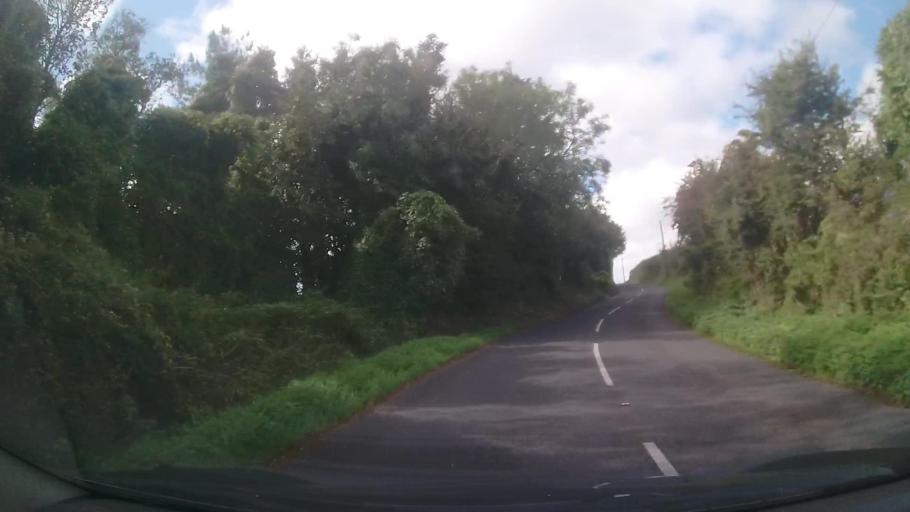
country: GB
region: Wales
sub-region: Pembrokeshire
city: Penally
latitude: 51.6554
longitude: -4.7593
